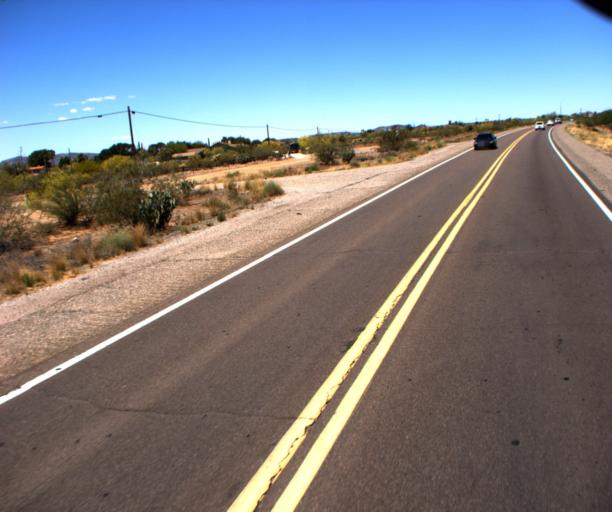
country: US
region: Arizona
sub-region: Maricopa County
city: Wickenburg
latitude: 33.9999
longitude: -112.7637
